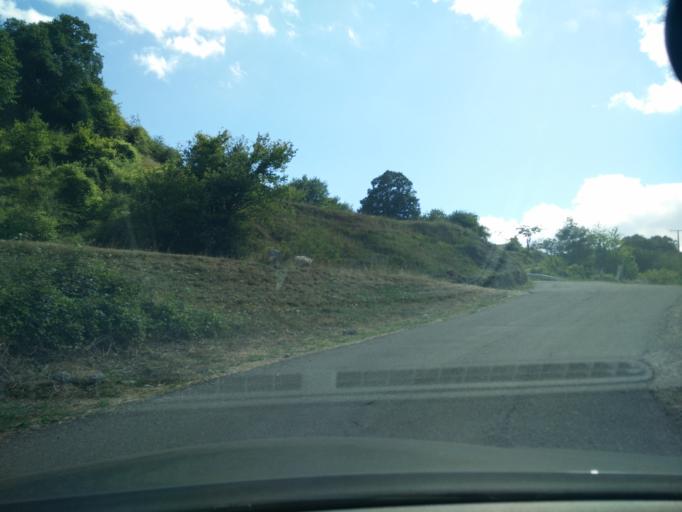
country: ES
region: Castille and Leon
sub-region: Provincia de Leon
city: Posada de Valdeon
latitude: 43.1636
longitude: -4.9092
